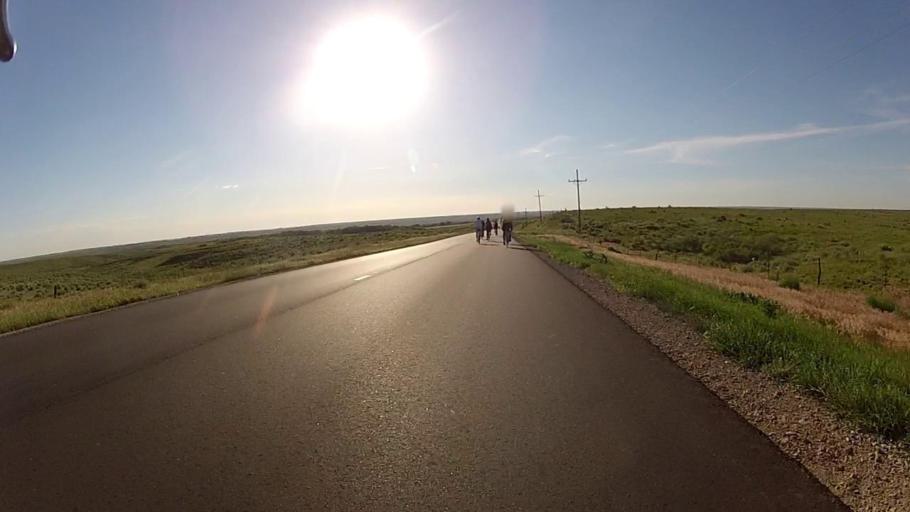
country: US
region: Kansas
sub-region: Comanche County
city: Coldwater
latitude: 37.2821
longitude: -99.0990
